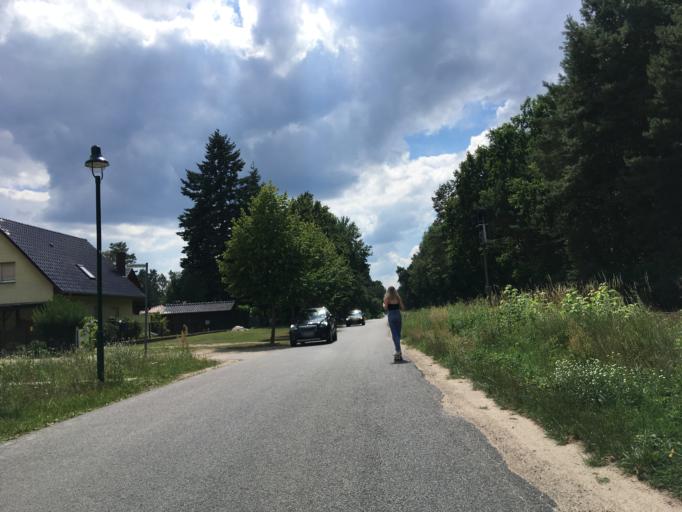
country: DE
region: Brandenburg
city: Wandlitz
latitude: 52.7405
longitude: 13.4612
